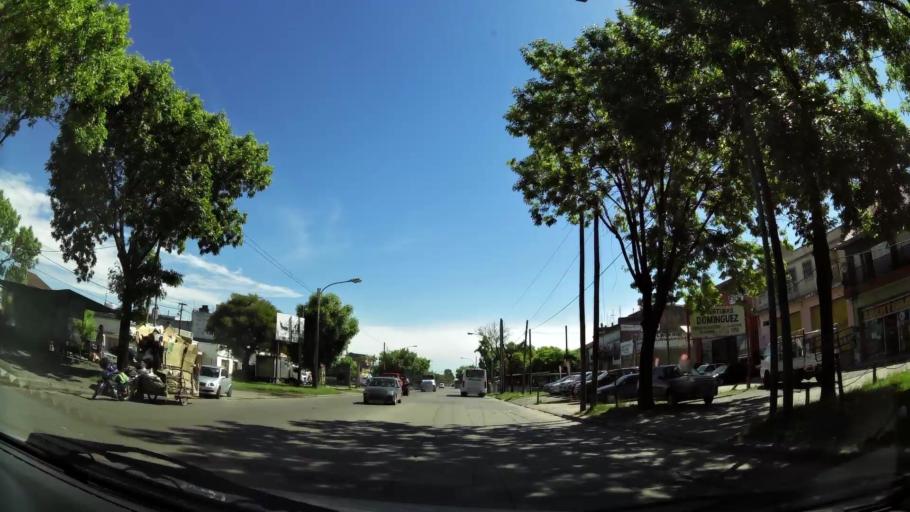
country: AR
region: Buenos Aires
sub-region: Partido de Almirante Brown
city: Adrogue
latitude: -34.7561
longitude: -58.3508
